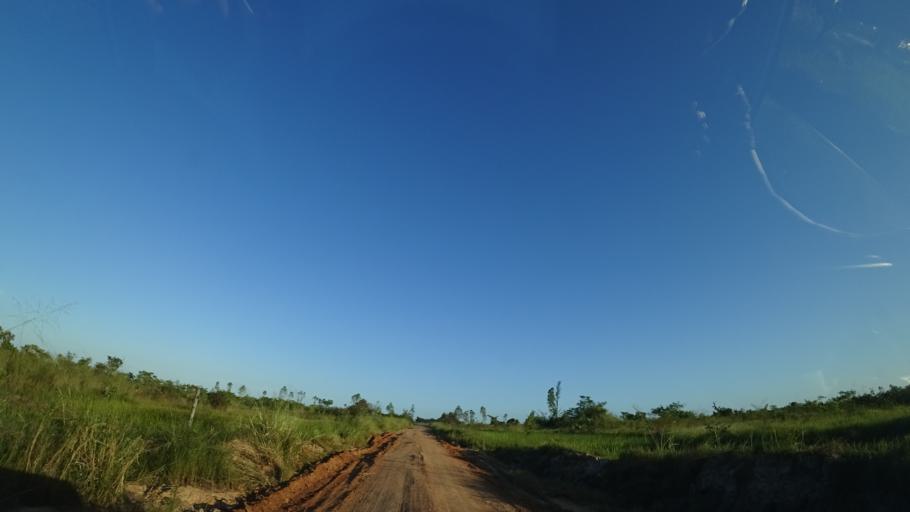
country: MZ
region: Sofala
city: Dondo
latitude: -19.4266
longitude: 34.7078
